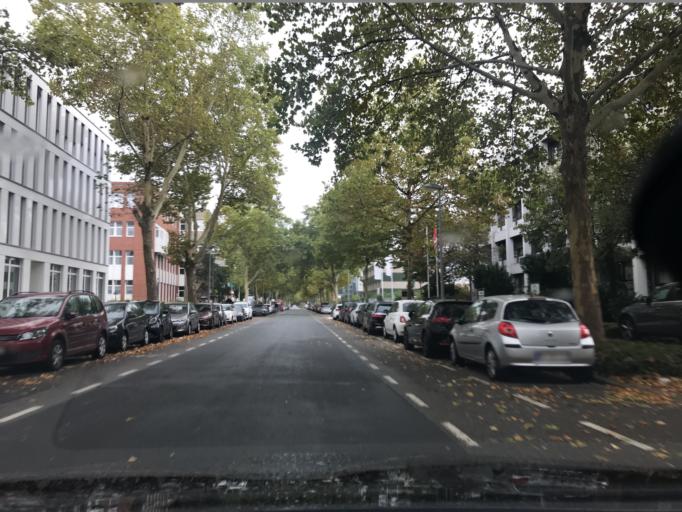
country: DE
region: North Rhine-Westphalia
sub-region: Regierungsbezirk Dusseldorf
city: Meerbusch
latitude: 51.2419
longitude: 6.7216
